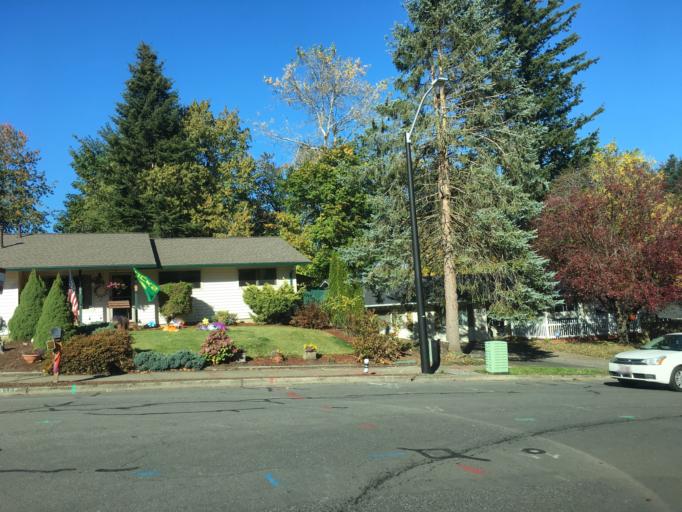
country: US
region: Oregon
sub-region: Multnomah County
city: Gresham
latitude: 45.5011
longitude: -122.4010
